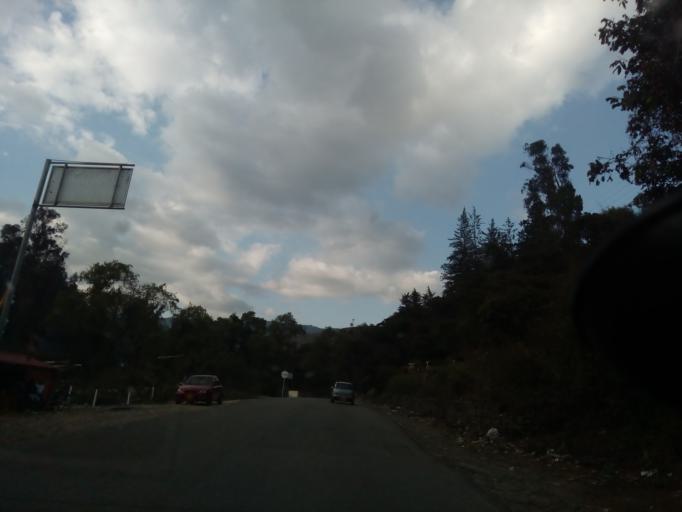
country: CO
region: Boyaca
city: Ramiriqui
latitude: 5.4185
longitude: -73.3477
